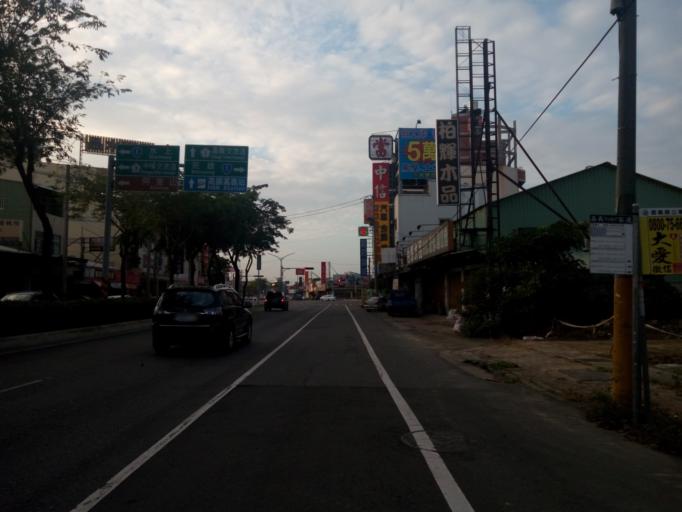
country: TW
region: Taiwan
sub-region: Chiayi
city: Jiayi Shi
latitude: 23.4838
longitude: 120.4239
